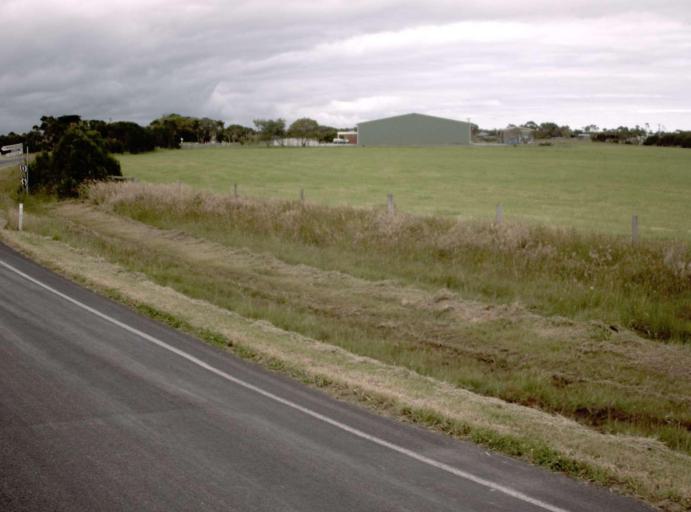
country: AU
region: Victoria
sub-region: Bass Coast
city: North Wonthaggi
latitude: -38.5794
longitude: 145.6322
